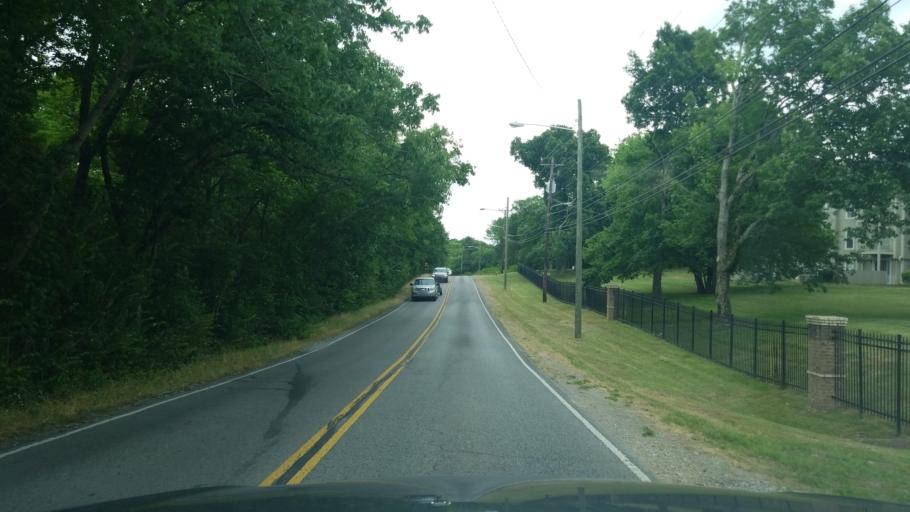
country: US
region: Tennessee
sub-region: Rutherford County
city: La Vergne
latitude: 36.0875
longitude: -86.6055
